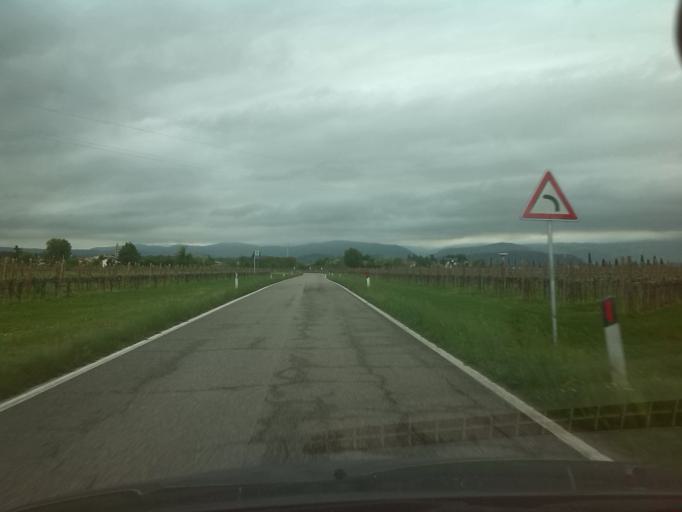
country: IT
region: Friuli Venezia Giulia
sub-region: Provincia di Gorizia
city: San Lorenzo Isontino
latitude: 45.9214
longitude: 13.5190
